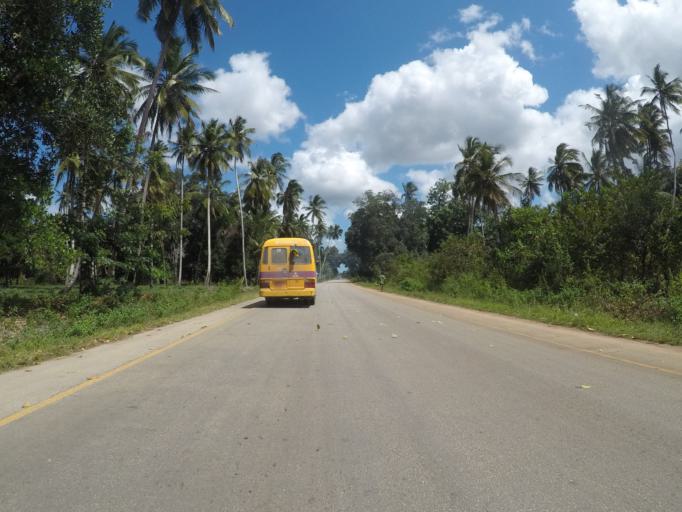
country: TZ
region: Zanzibar Central/South
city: Koani
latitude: -6.1512
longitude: 39.3296
